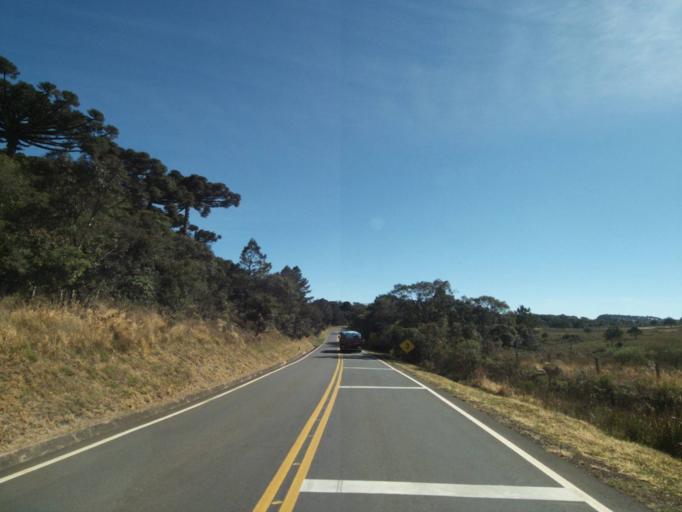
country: BR
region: Parana
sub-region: Castro
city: Castro
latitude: -24.7298
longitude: -50.1833
